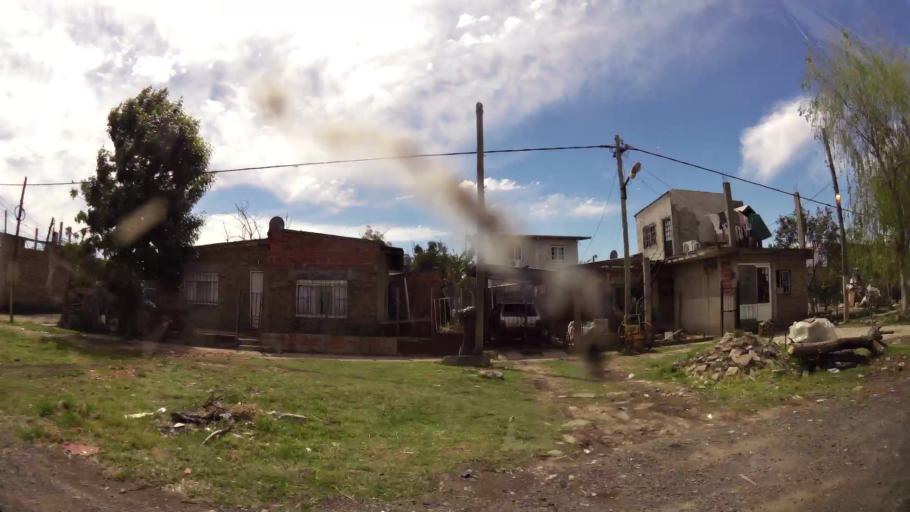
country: AR
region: Buenos Aires
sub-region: Partido de Quilmes
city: Quilmes
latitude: -34.7592
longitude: -58.3025
